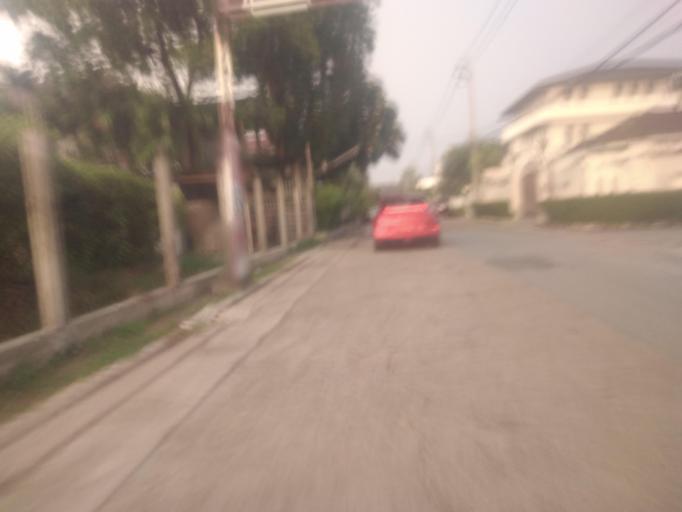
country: TH
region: Bangkok
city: Phasi Charoen
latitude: 13.7422
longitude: 100.4444
